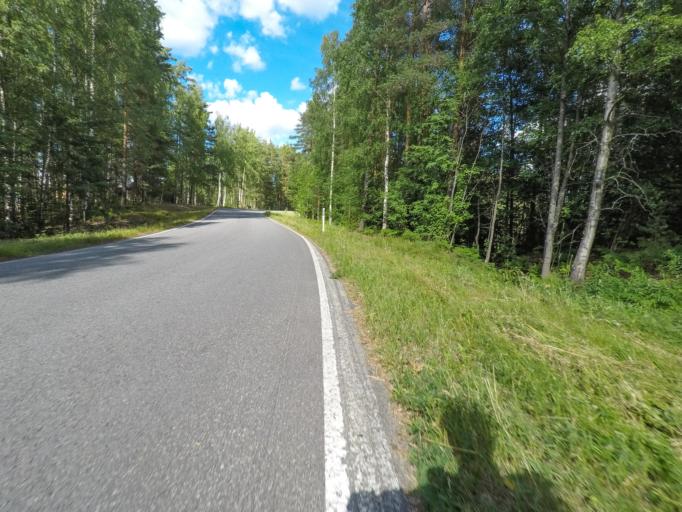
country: FI
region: South Karelia
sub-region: Lappeenranta
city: Joutseno
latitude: 61.1189
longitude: 28.3807
